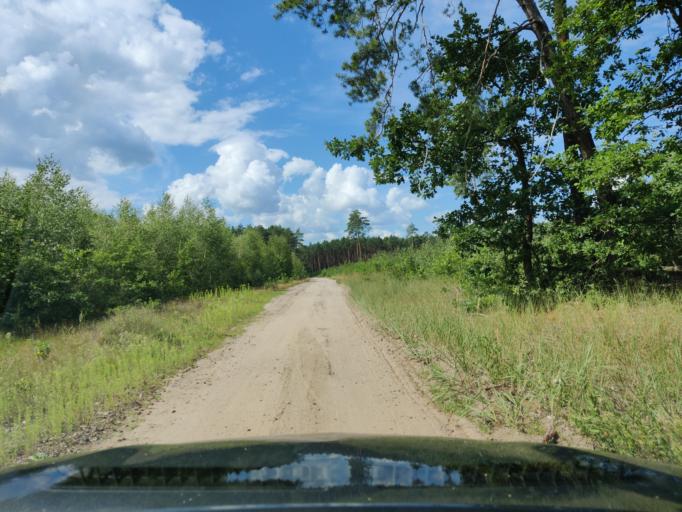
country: PL
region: Masovian Voivodeship
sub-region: Powiat pultuski
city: Obryte
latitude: 52.7443
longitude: 21.1830
